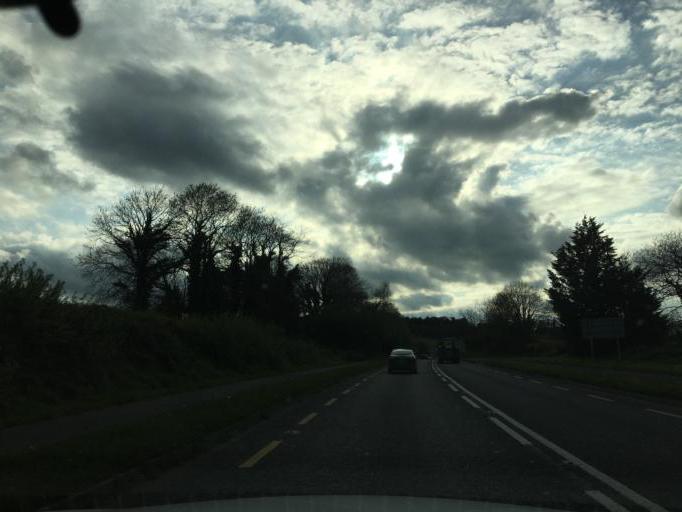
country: IE
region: Leinster
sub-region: Loch Garman
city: Loch Garman
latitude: 52.3376
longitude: -6.5182
